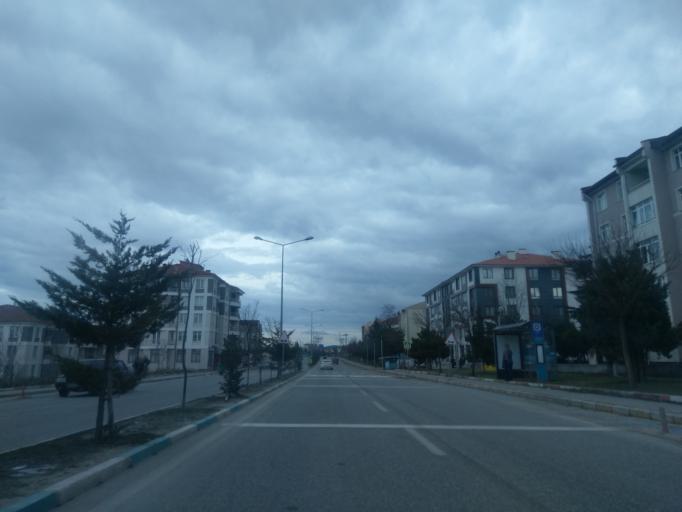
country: TR
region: Kuetahya
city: Kutahya
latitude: 39.3924
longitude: 30.0325
